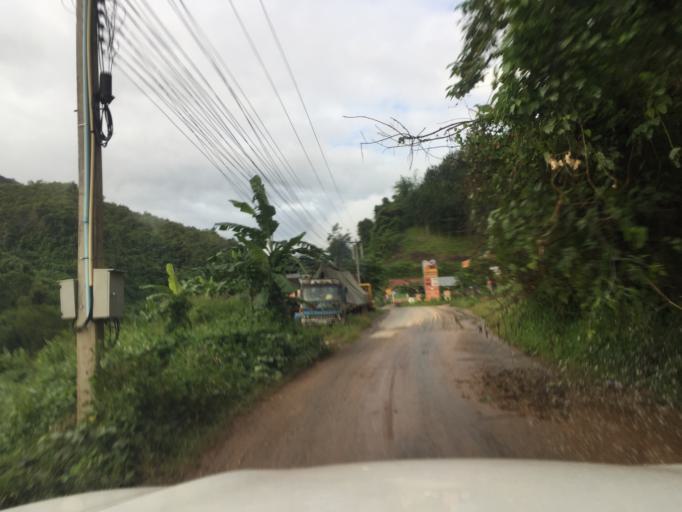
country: LA
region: Phongsali
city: Khoa
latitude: 21.0970
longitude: 102.2511
